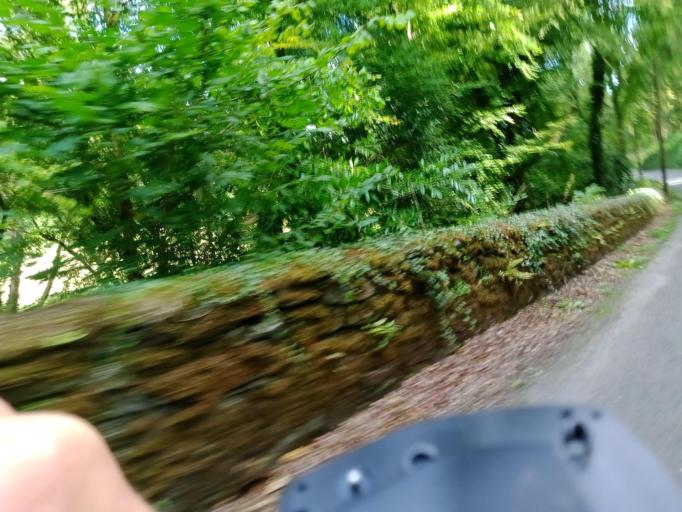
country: IE
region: Munster
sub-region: Waterford
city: Dungarvan
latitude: 52.1234
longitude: -7.4679
